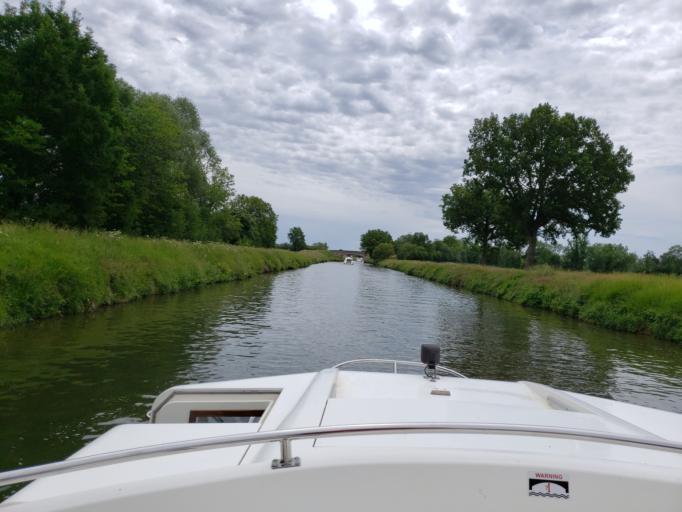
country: FR
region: Bourgogne
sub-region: Departement de l'Yonne
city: Gurgy
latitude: 47.8825
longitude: 3.5469
